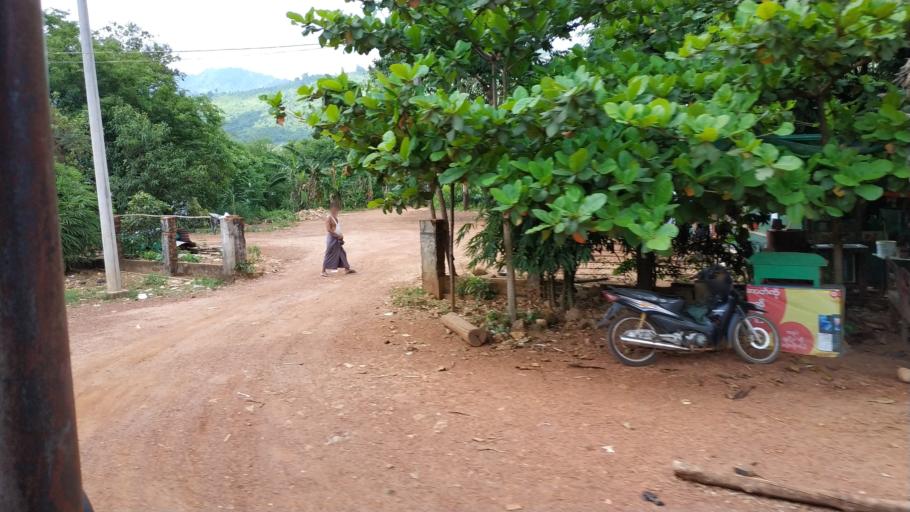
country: MM
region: Mon
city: Kyaikto
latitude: 17.4039
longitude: 97.0762
